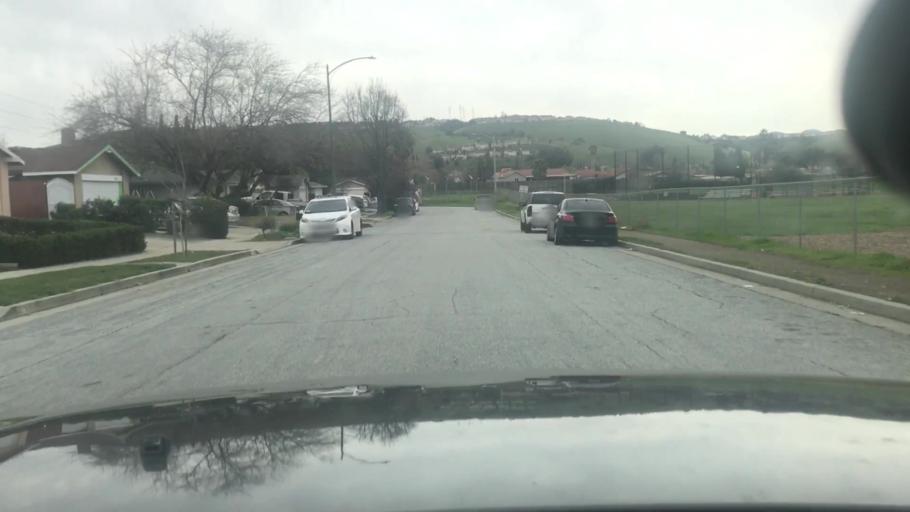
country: US
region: California
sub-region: Santa Clara County
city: Seven Trees
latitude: 37.3041
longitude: -121.8031
